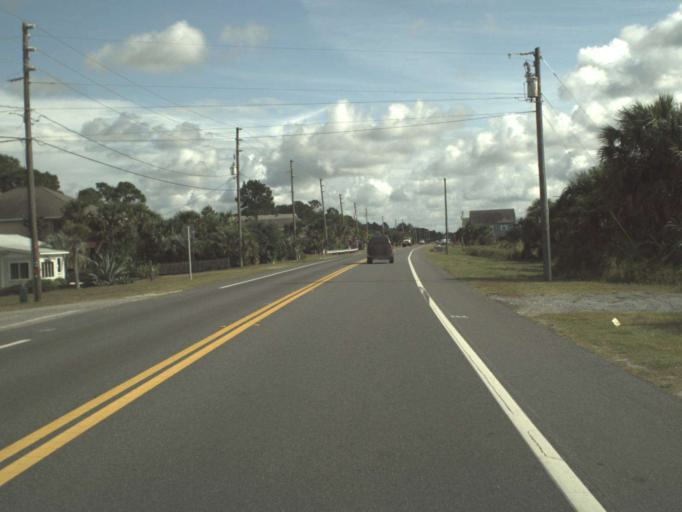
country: US
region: Florida
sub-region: Bay County
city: Mexico Beach
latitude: 29.8981
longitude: -85.3624
